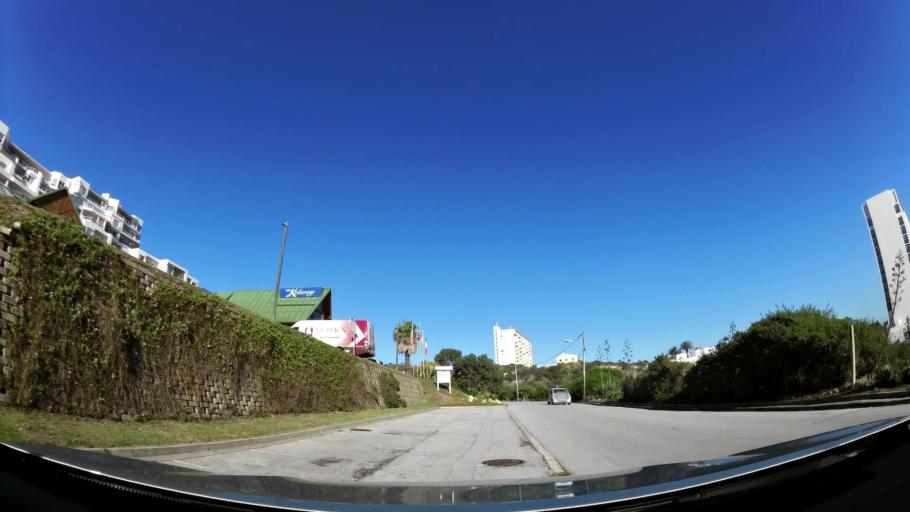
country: ZA
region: Eastern Cape
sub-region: Nelson Mandela Bay Metropolitan Municipality
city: Port Elizabeth
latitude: -33.9785
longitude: 25.6484
